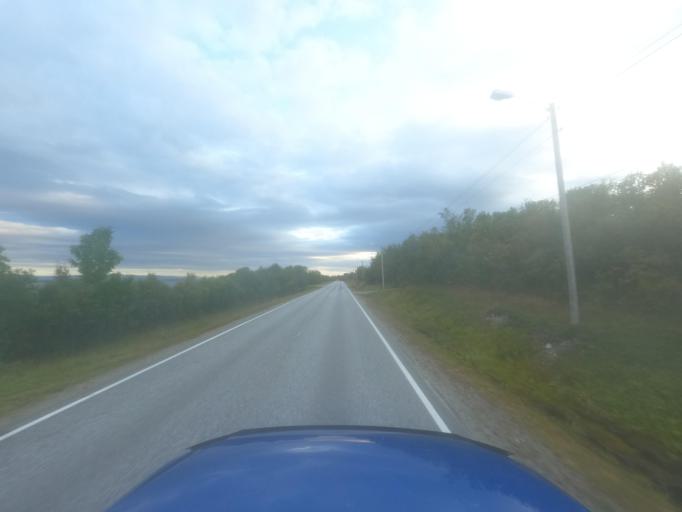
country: NO
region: Finnmark Fylke
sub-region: Porsanger
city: Lakselv
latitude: 70.4512
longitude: 25.2216
